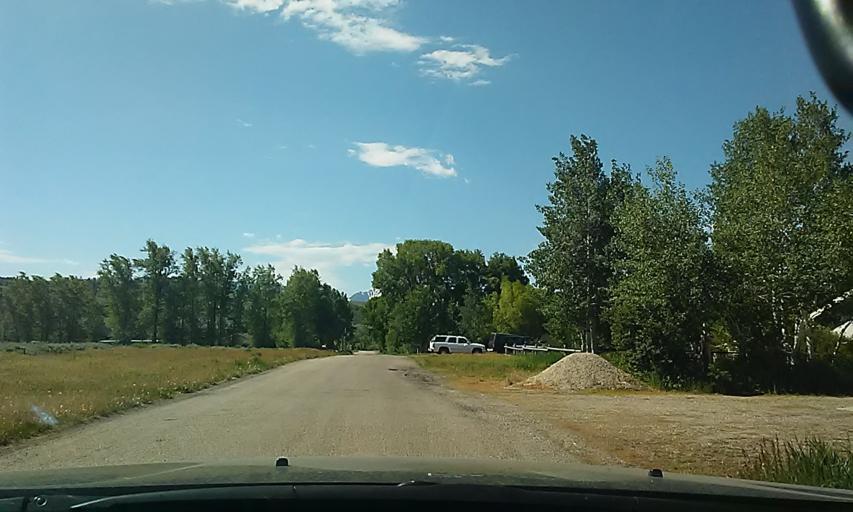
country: US
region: Wyoming
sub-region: Teton County
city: Jackson
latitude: 43.6241
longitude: -110.6239
